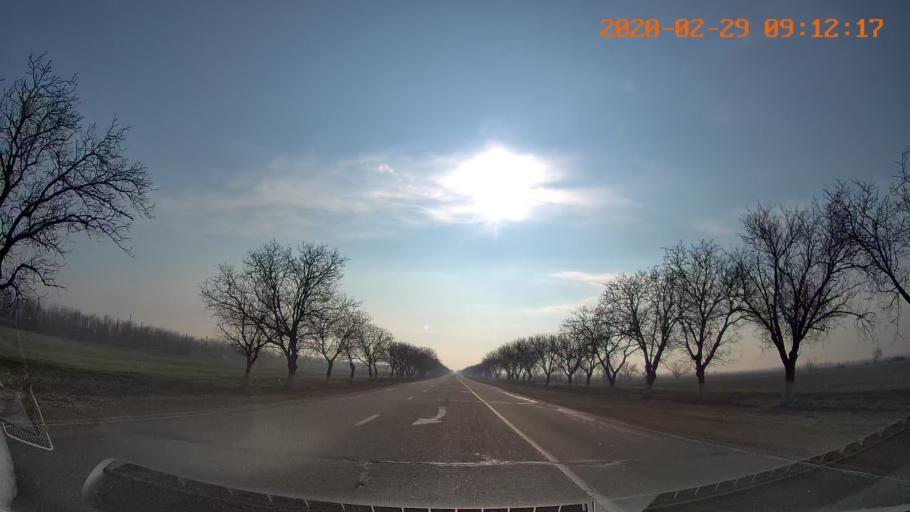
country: MD
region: Telenesti
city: Slobozia
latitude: 46.8279
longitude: 29.8143
